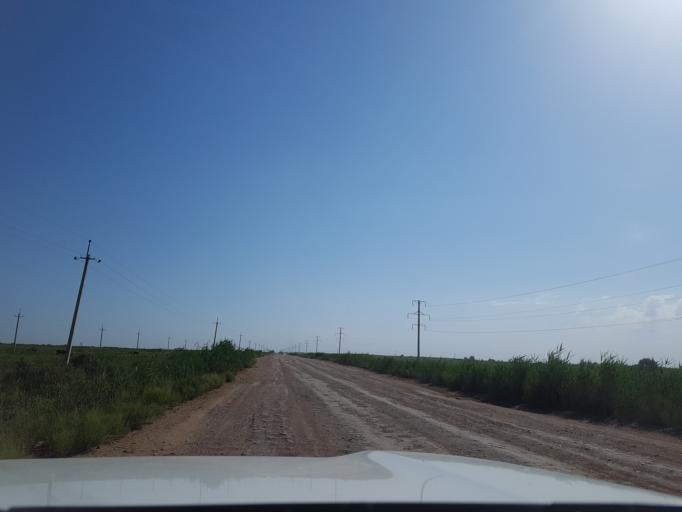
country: TM
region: Dasoguz
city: Koeneuergench
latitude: 42.1139
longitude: 58.9218
